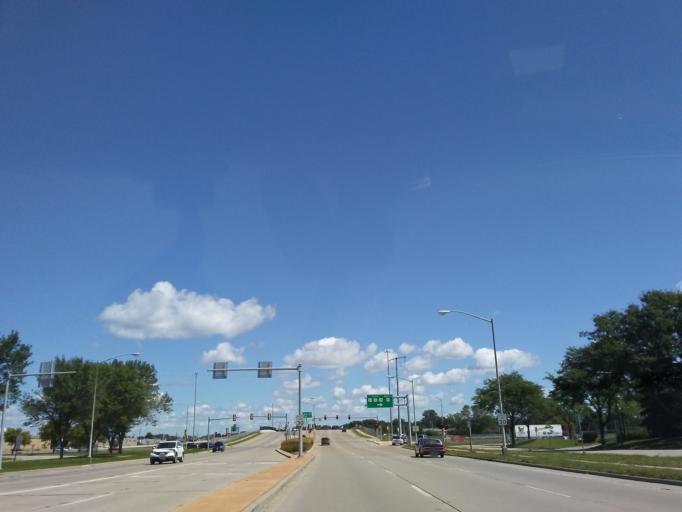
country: US
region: Wisconsin
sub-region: Dane County
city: Madison
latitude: 43.0320
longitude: -89.4086
